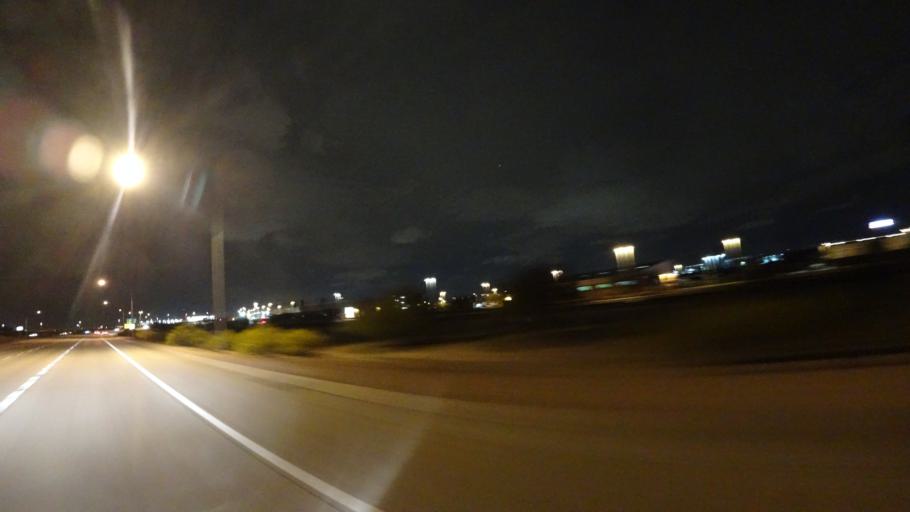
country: US
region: Arizona
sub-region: Maricopa County
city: Tempe Junction
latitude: 33.4388
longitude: -111.9691
